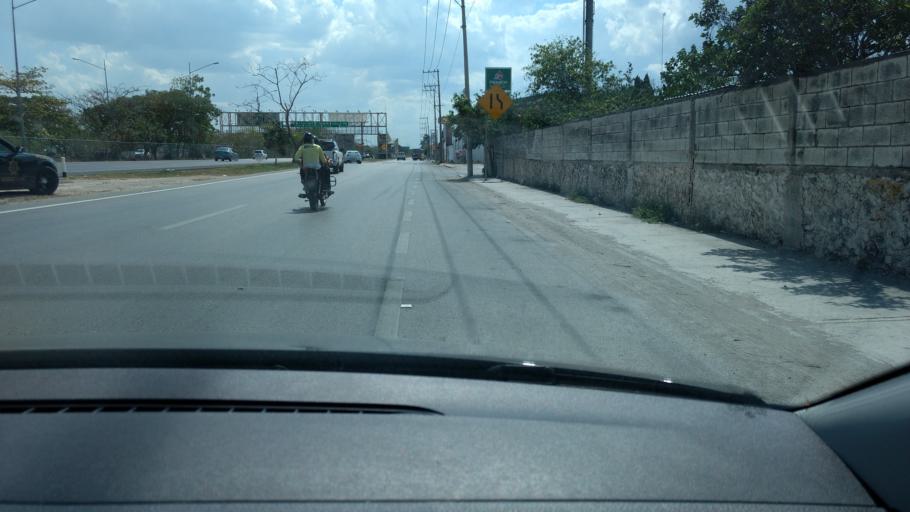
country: MX
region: Yucatan
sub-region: Kanasin
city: Kanasin
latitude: 20.9765
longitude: -89.5649
